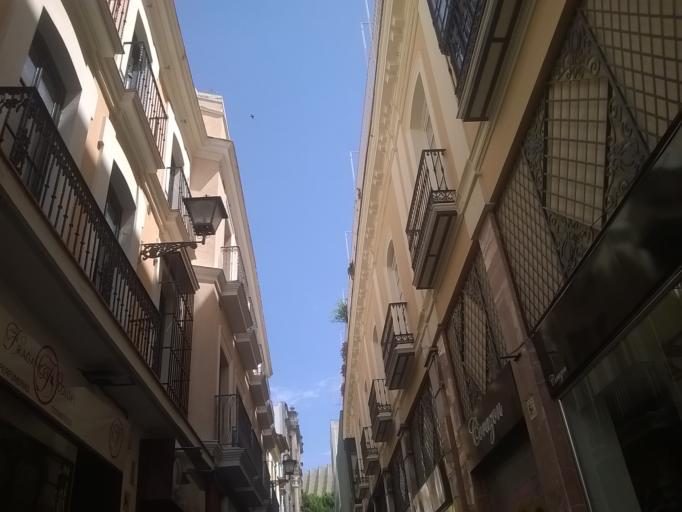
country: ES
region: Andalusia
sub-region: Provincia de Sevilla
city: Sevilla
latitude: 37.3914
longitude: -5.9921
